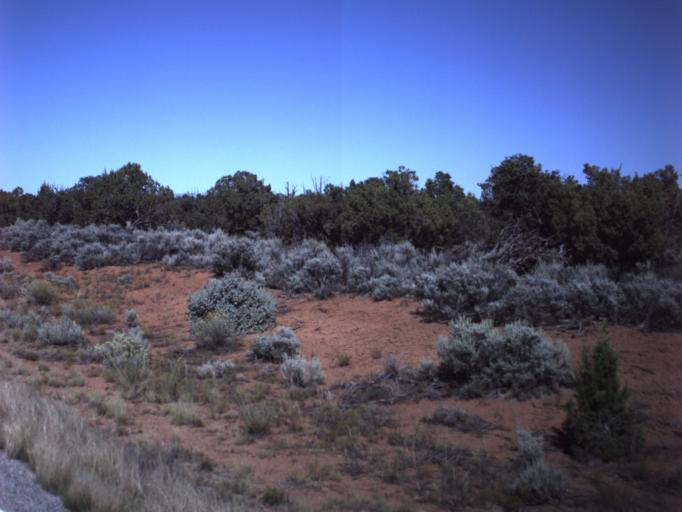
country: US
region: Utah
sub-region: San Juan County
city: Blanding
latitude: 37.3439
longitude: -109.9151
